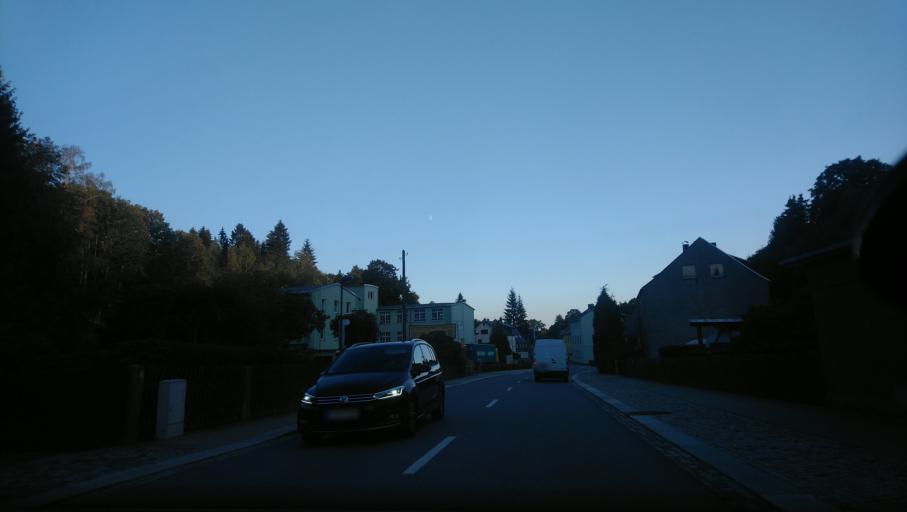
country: DE
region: Saxony
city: Geyer
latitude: 50.6211
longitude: 12.9248
